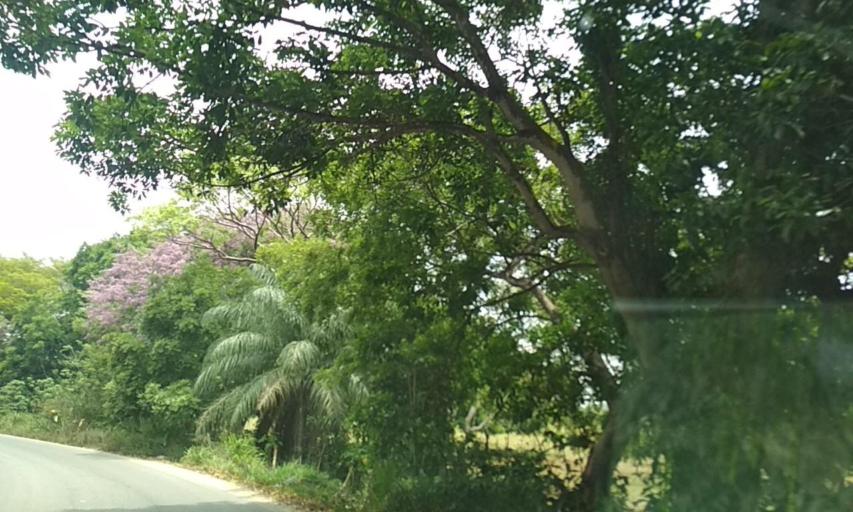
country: MX
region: Veracruz
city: Las Choapas
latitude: 17.8639
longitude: -94.0982
